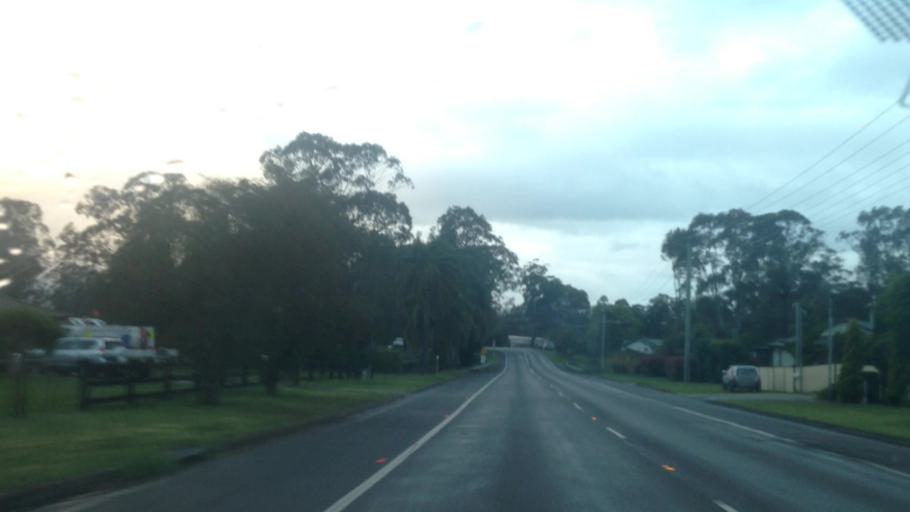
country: AU
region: New South Wales
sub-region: Lake Macquarie Shire
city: Cooranbong
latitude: -33.0850
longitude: 151.4484
